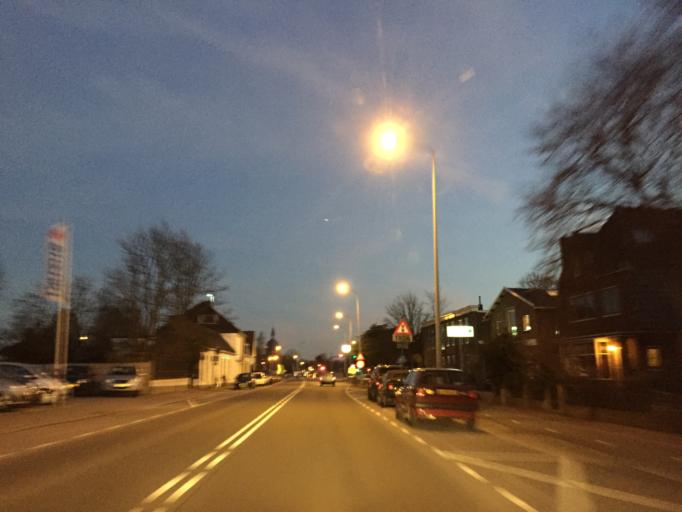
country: NL
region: South Holland
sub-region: Gemeente Leiderdorp
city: Leiderdorp
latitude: 52.1494
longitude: 4.5218
